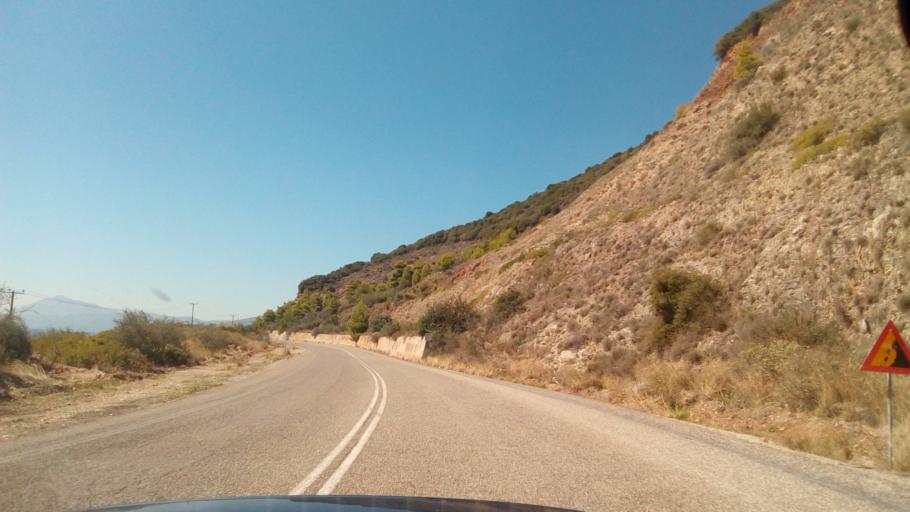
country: GR
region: West Greece
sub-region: Nomos Achaias
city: Kamarai
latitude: 38.4052
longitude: 21.9699
